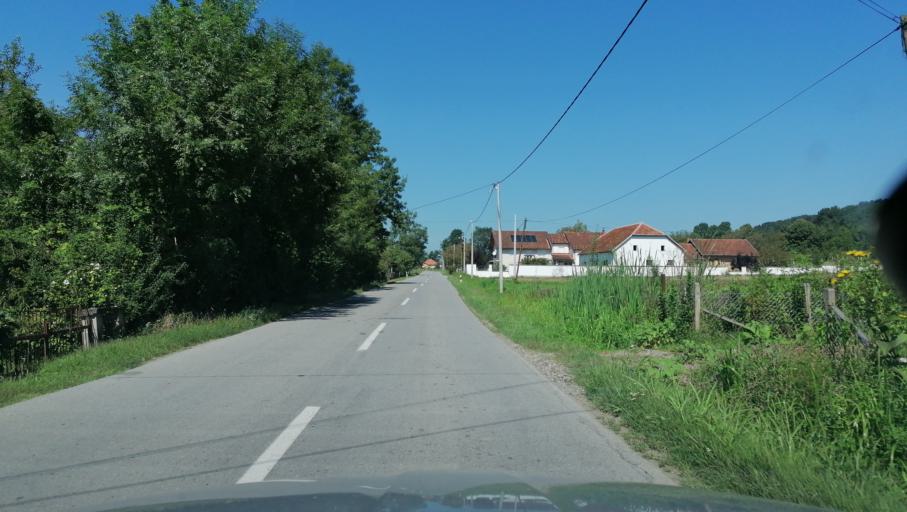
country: RS
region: Central Serbia
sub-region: Raski Okrug
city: Vrnjacka Banja
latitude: 43.6955
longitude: 20.8602
